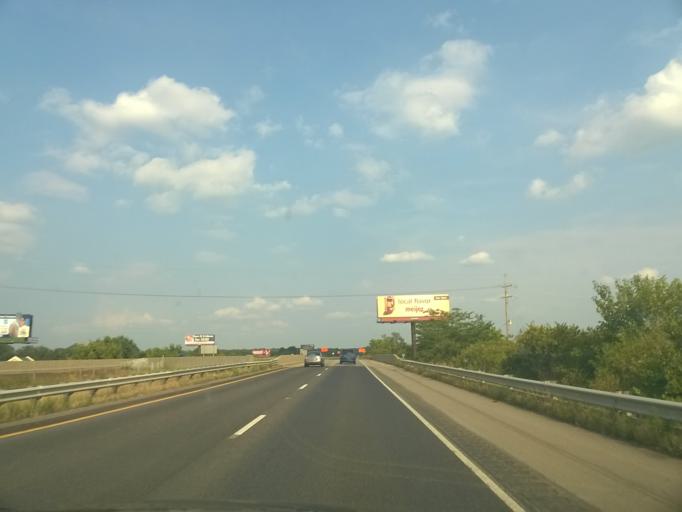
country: US
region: Indiana
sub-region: Vigo County
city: Terre Haute
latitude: 39.4313
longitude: -87.3930
